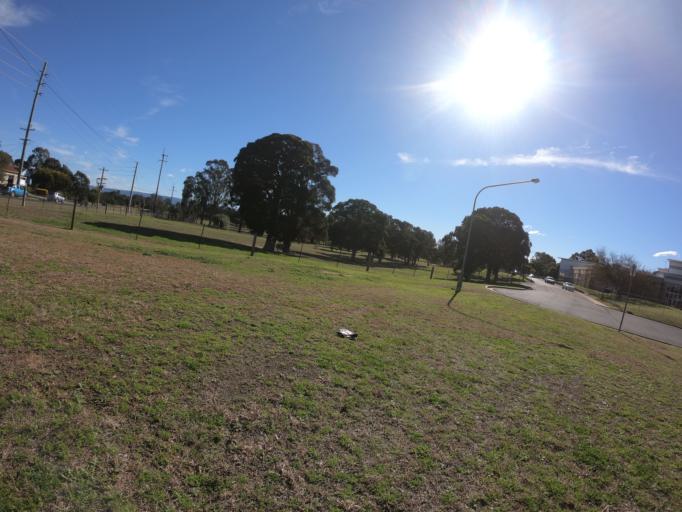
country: AU
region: New South Wales
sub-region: Hawkesbury
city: South Windsor
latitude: -33.6227
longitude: 150.7999
